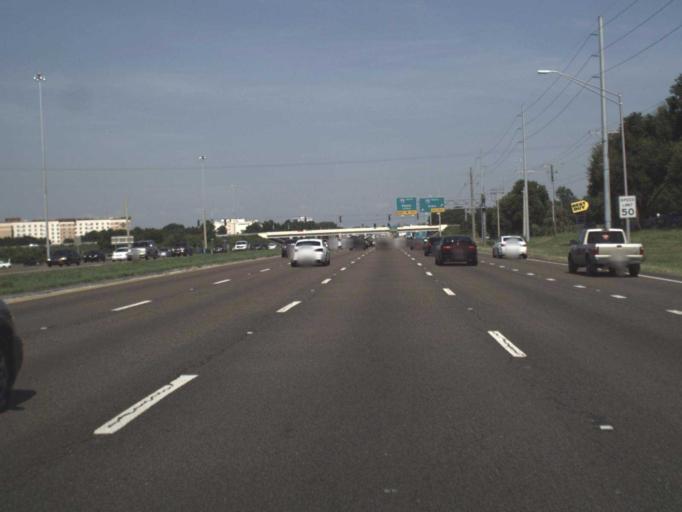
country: US
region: Florida
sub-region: Hillsborough County
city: Brandon
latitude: 27.9398
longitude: -82.3246
